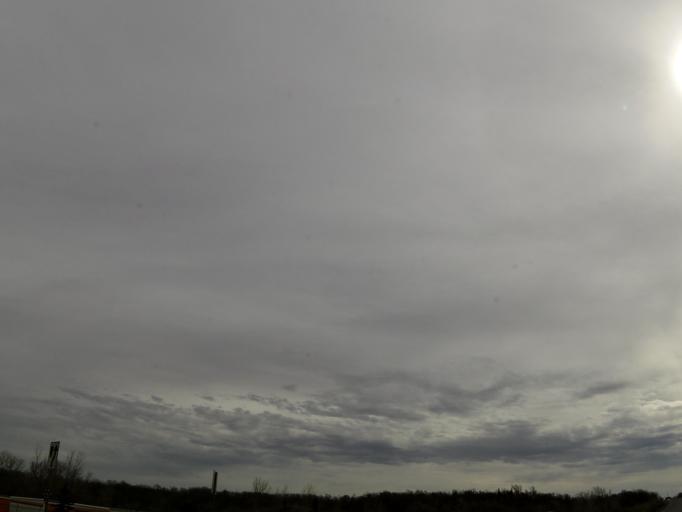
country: US
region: Minnesota
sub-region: Scott County
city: Savage
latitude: 44.7717
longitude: -93.3791
